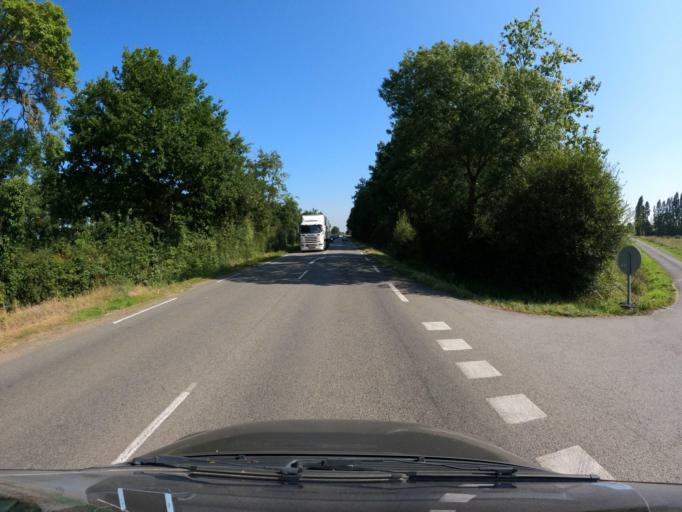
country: FR
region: Pays de la Loire
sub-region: Departement de la Loire-Atlantique
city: Pont-Saint-Martin
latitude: 47.1015
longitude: -1.5514
